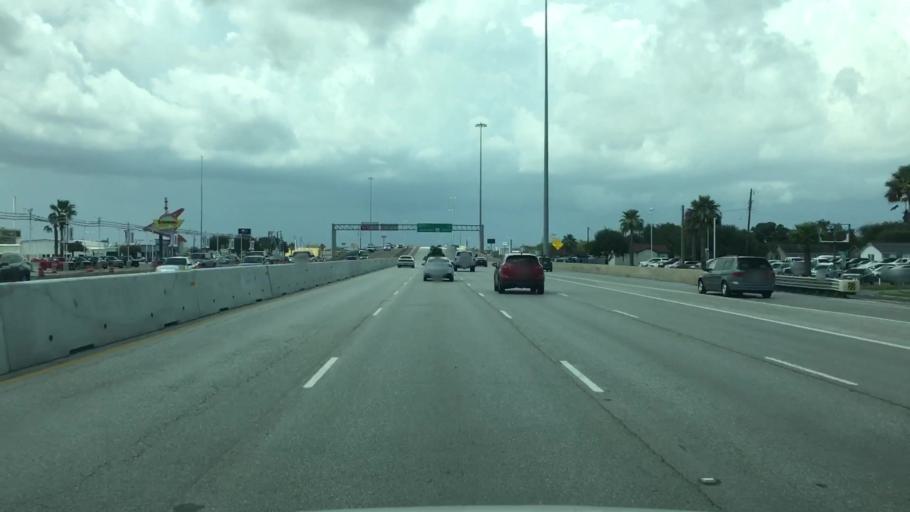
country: US
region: Texas
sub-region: Nueces County
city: Corpus Christi
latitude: 27.7232
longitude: -97.4017
